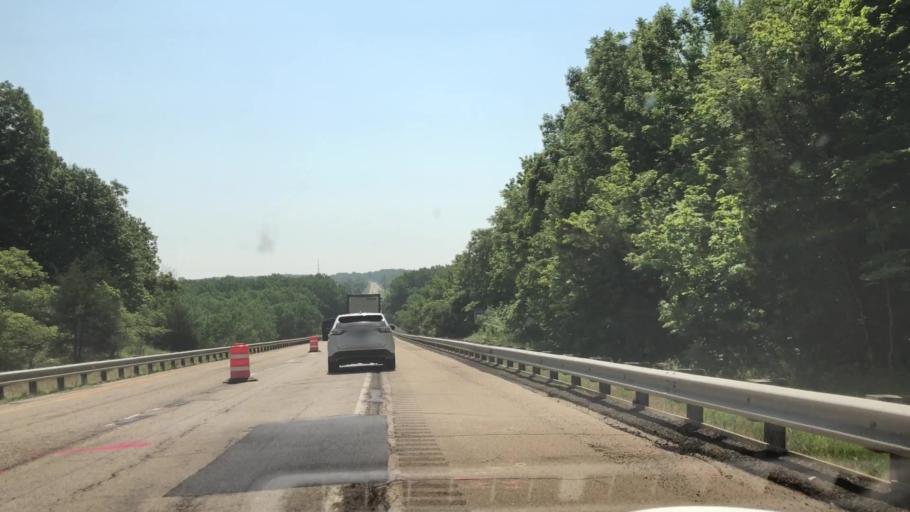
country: US
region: Illinois
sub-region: Woodford County
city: Eureka
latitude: 40.6158
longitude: -89.2566
